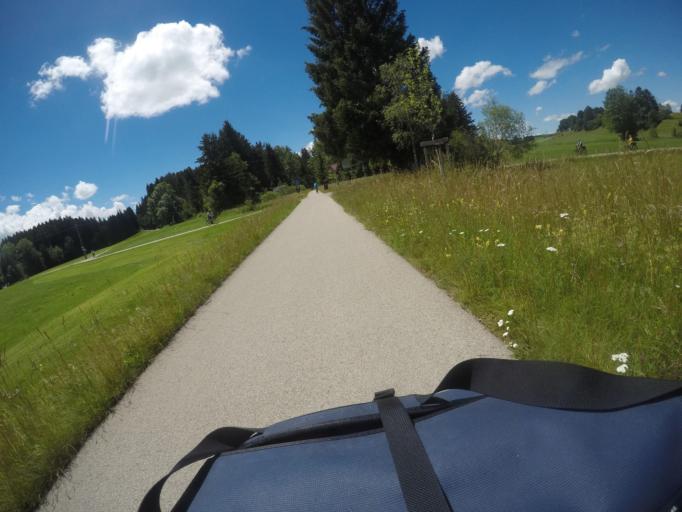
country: DE
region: Bavaria
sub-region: Upper Bavaria
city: Prem
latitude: 47.6803
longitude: 10.7539
